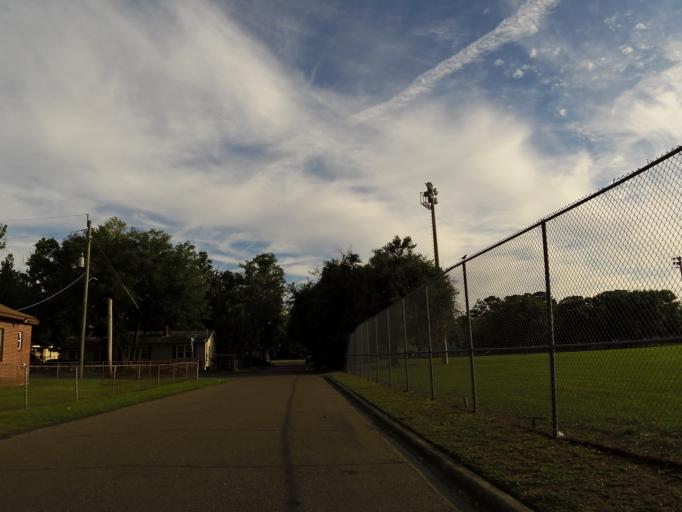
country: US
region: Florida
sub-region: Duval County
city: Jacksonville
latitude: 30.3581
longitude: -81.6624
